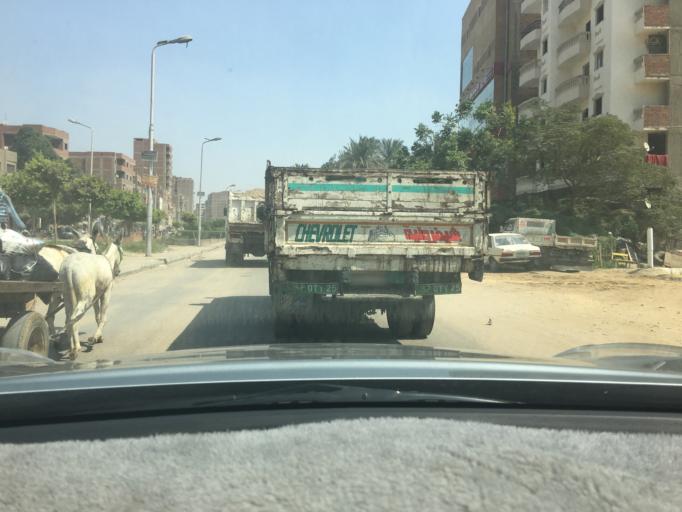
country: EG
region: Muhafazat al Qalyubiyah
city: Al Khankah
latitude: 30.1409
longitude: 31.3480
